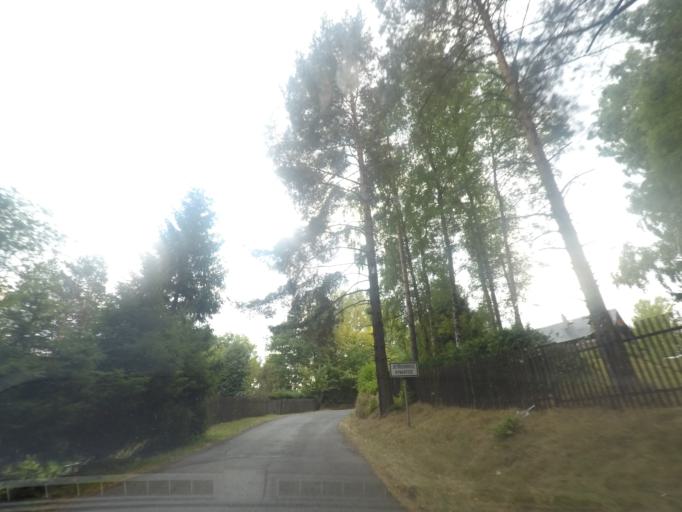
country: CZ
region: Ustecky
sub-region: Okres Decin
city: Chribska
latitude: 50.8550
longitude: 14.4270
